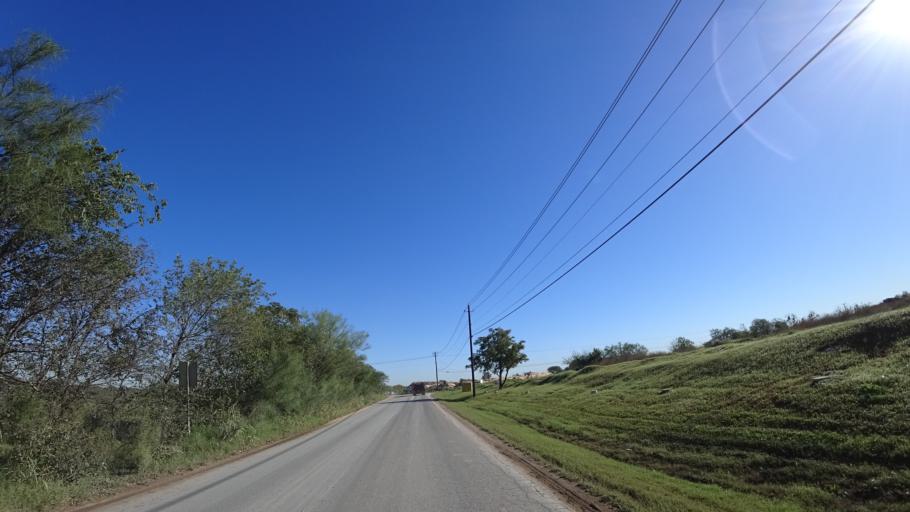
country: US
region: Texas
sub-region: Travis County
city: Hornsby Bend
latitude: 30.2369
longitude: -97.6632
